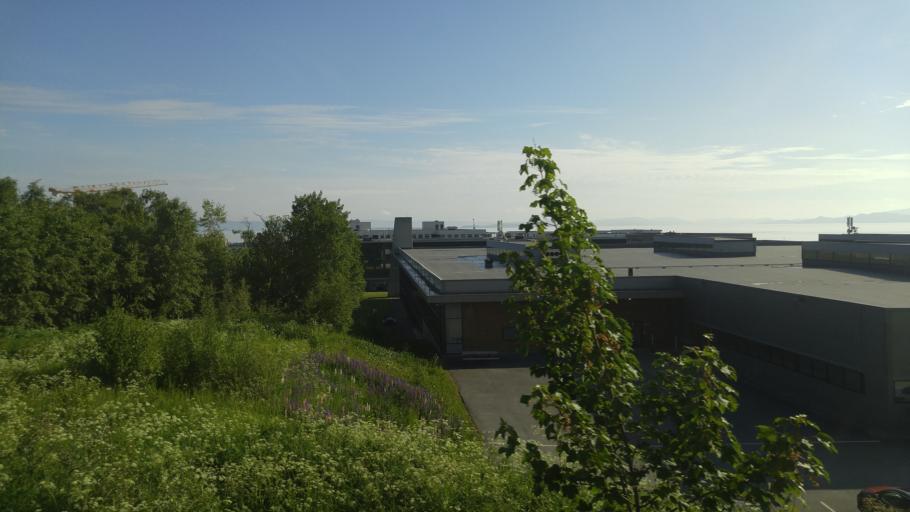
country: NO
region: Sor-Trondelag
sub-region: Trondheim
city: Trondheim
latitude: 63.4317
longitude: 10.5056
